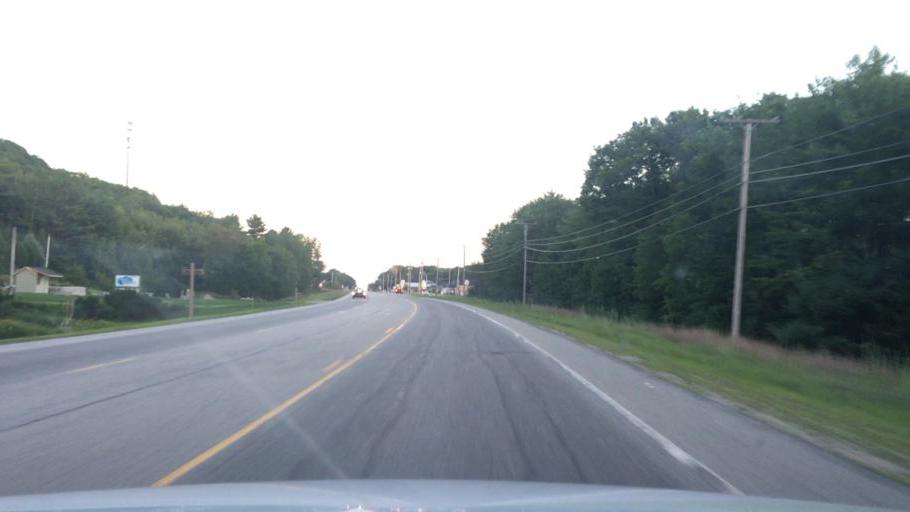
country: US
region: Maine
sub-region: Androscoggin County
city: Turner
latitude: 44.2011
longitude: -70.2450
